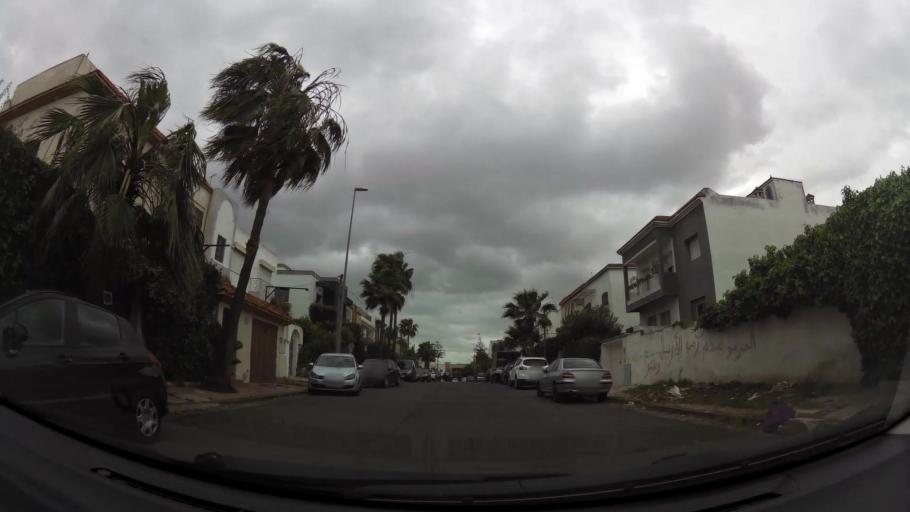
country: MA
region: Grand Casablanca
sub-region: Casablanca
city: Casablanca
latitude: 33.5757
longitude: -7.6713
